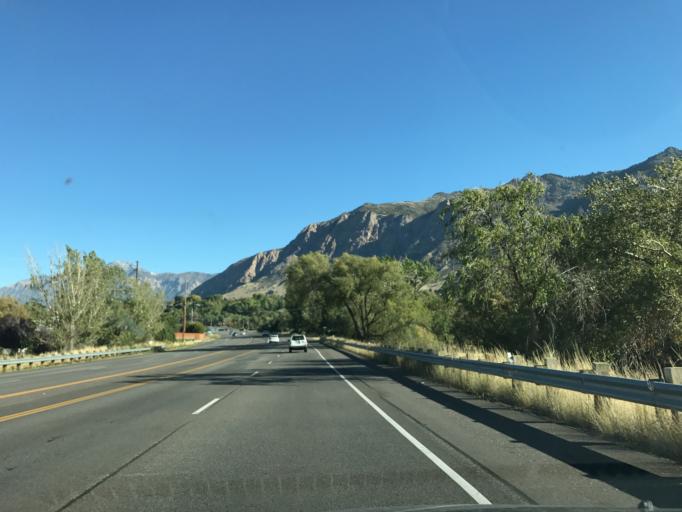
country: US
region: Utah
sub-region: Weber County
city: Ogden
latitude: 41.2372
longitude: -111.9460
